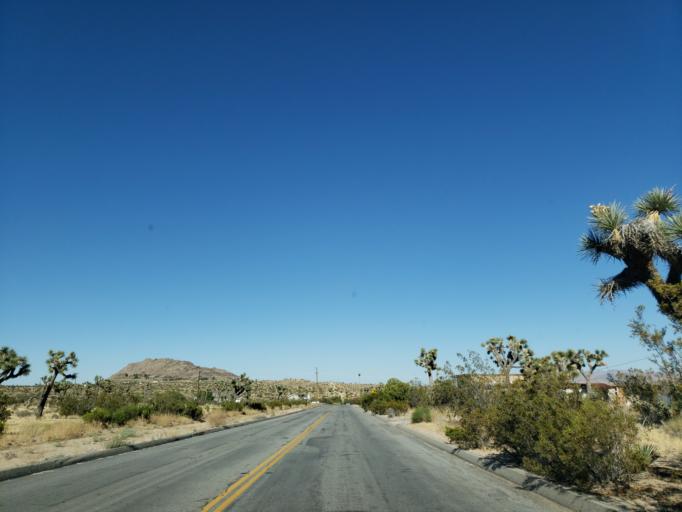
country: US
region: California
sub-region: San Bernardino County
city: Joshua Tree
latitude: 34.1640
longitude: -116.3722
